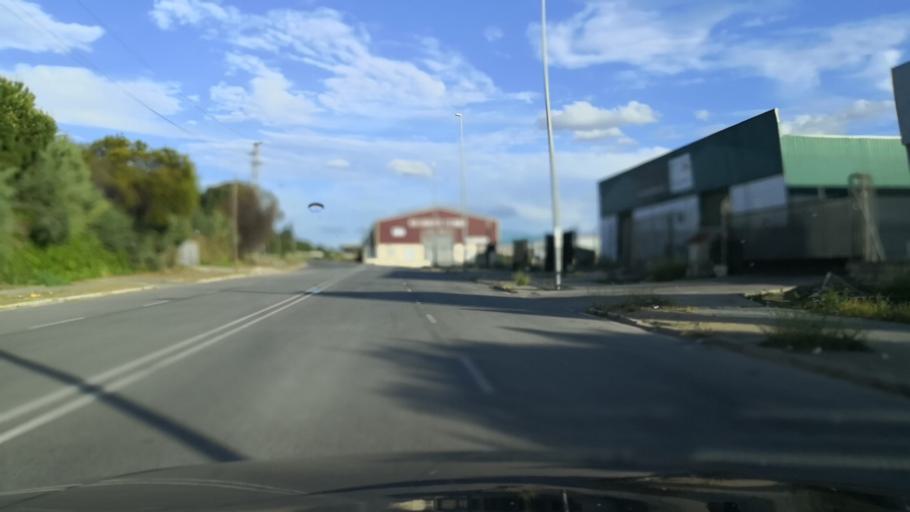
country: ES
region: Extremadura
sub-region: Provincia de Badajoz
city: Badajoz
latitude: 38.8979
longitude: -6.9878
